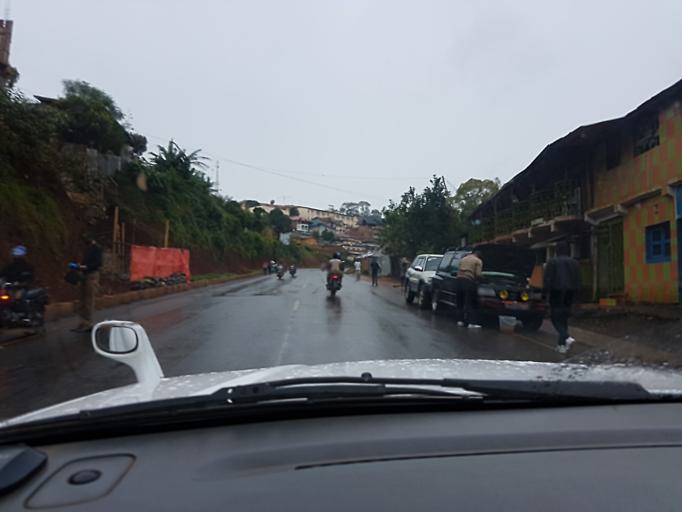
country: CD
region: South Kivu
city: Bukavu
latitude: -2.5057
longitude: 28.8540
